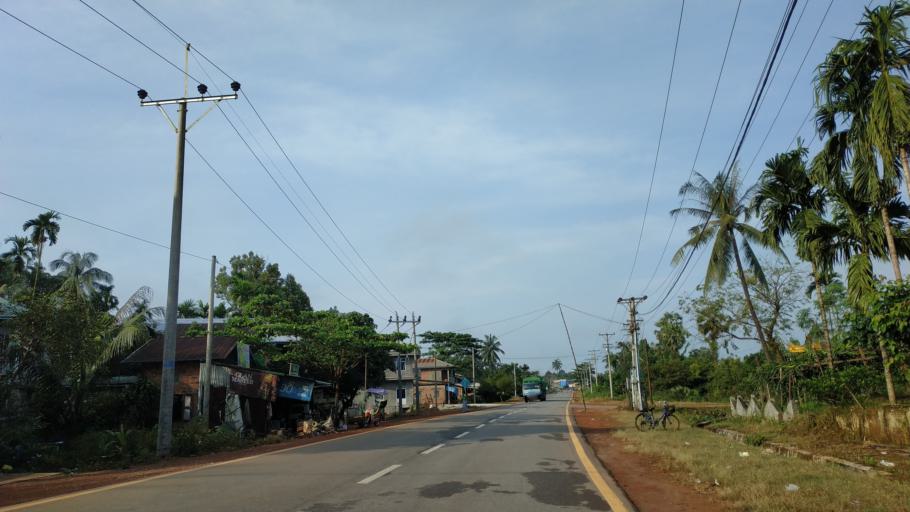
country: MM
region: Tanintharyi
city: Dawei
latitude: 14.2489
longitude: 98.2042
